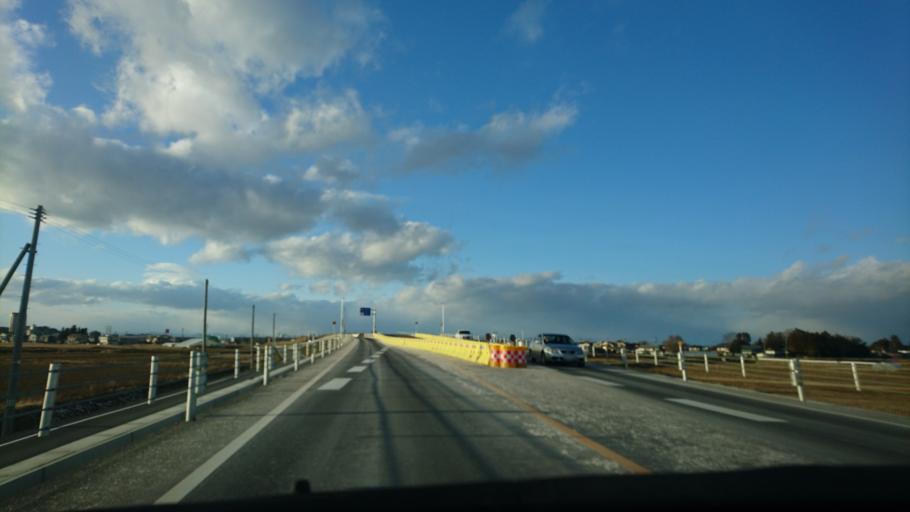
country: JP
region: Miyagi
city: Wakuya
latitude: 38.6929
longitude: 141.2167
